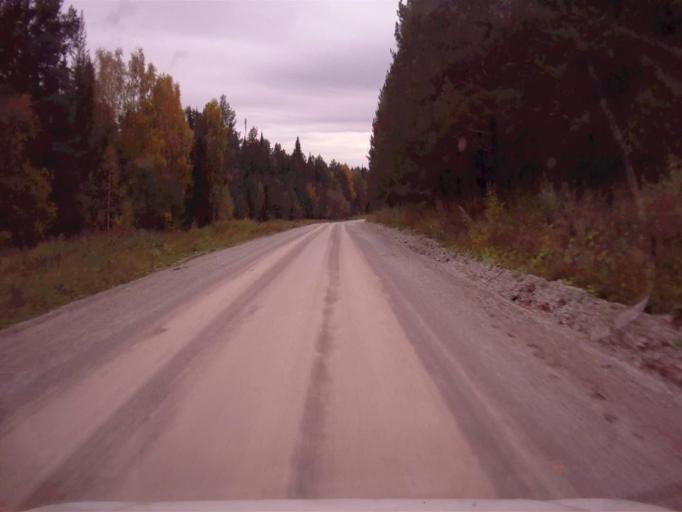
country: RU
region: Chelyabinsk
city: Nyazepetrovsk
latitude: 56.0506
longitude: 59.5314
